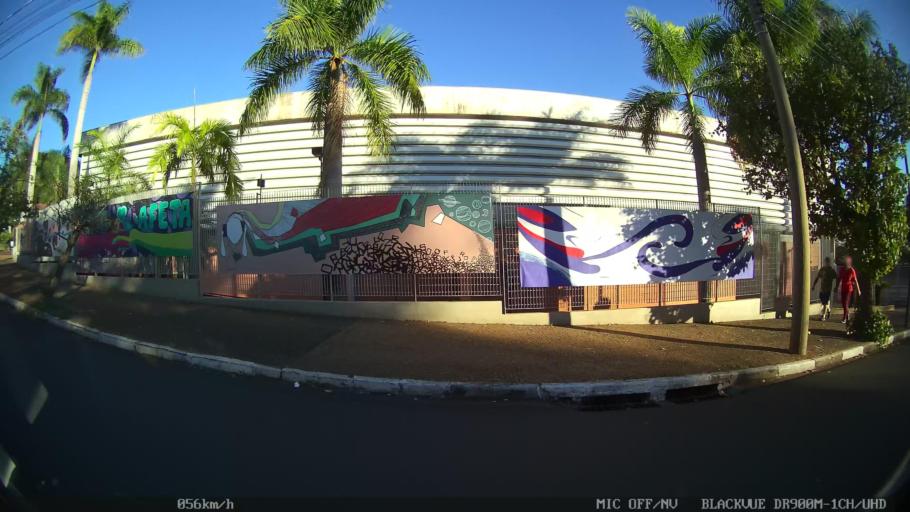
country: BR
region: Sao Paulo
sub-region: Araraquara
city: Araraquara
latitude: -21.8016
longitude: -48.1882
